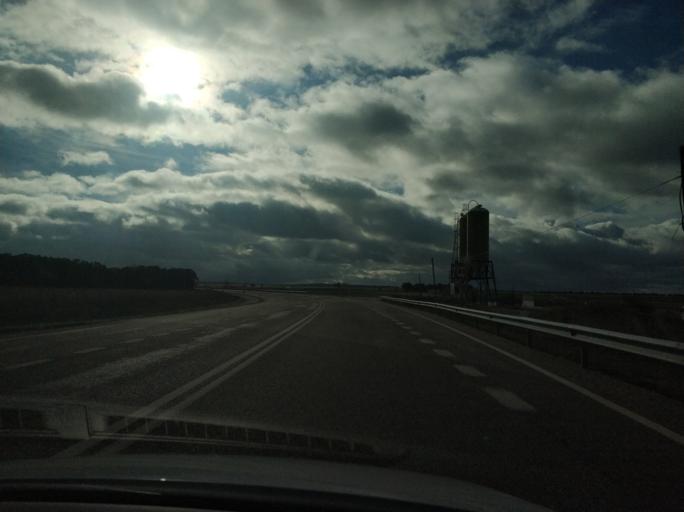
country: ES
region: Castille and Leon
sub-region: Provincia de Segovia
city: Languilla
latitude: 41.4081
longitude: -3.4162
